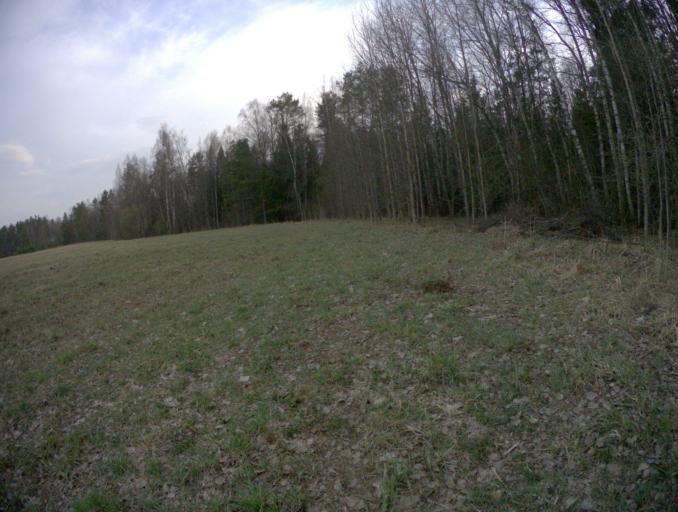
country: RU
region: Vladimir
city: Kommunar
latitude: 56.0765
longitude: 40.5277
